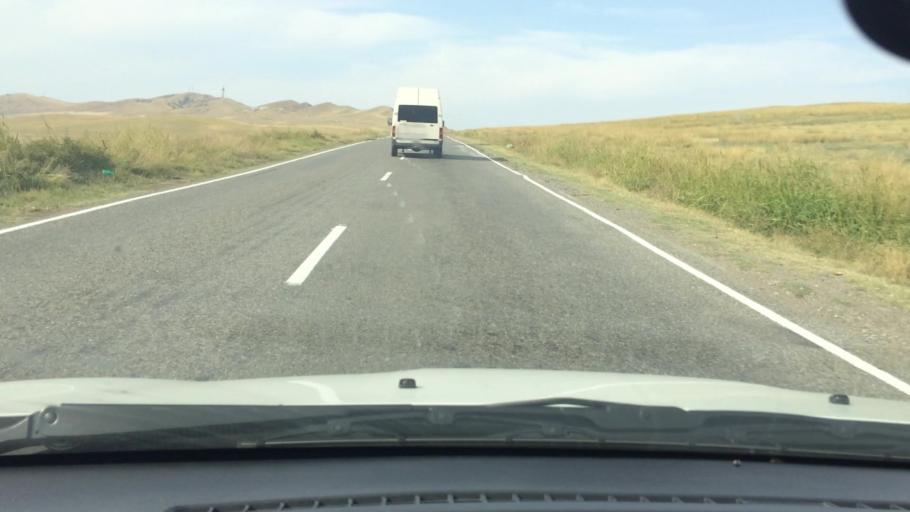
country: GE
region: Kvemo Kartli
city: Rust'avi
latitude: 41.5271
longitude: 44.9807
